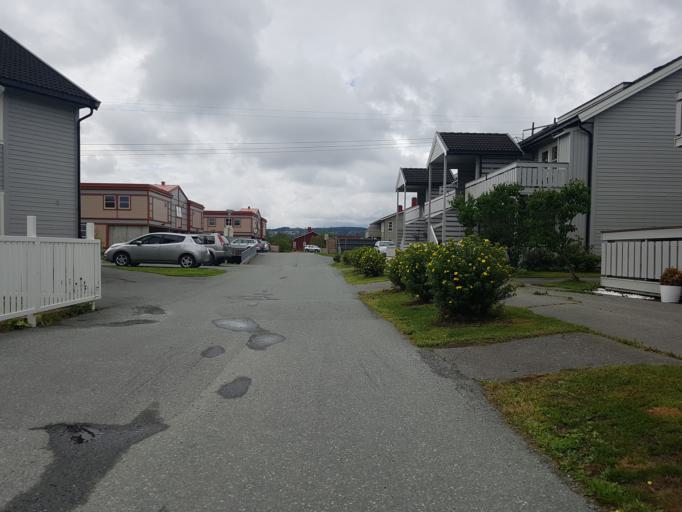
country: NO
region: Sor-Trondelag
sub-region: Trondheim
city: Trondheim
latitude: 63.3866
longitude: 10.3967
